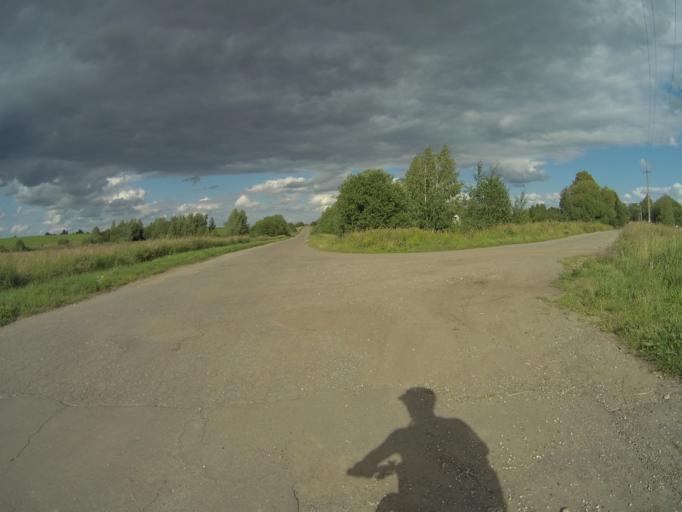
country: RU
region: Vladimir
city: Suzdal'
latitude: 56.3194
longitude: 40.4170
